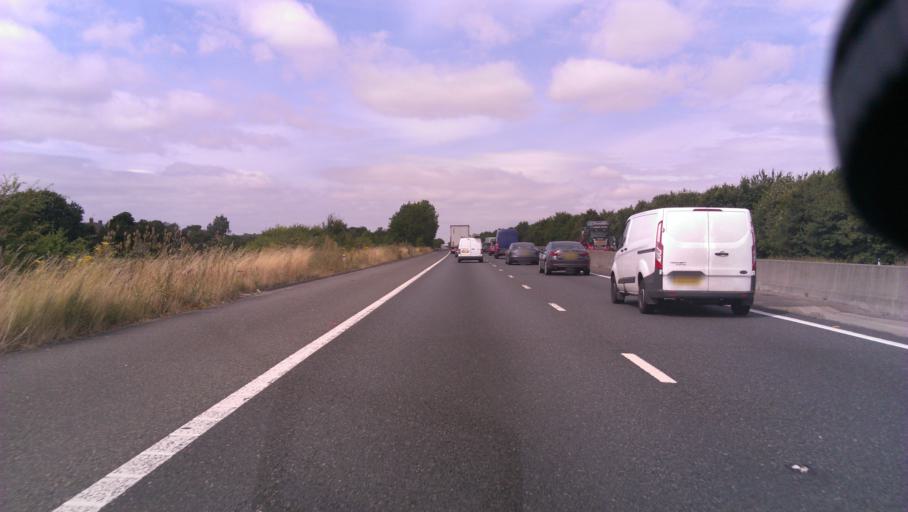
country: GB
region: England
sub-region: Essex
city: Elsenham
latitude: 51.9470
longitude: 0.2158
